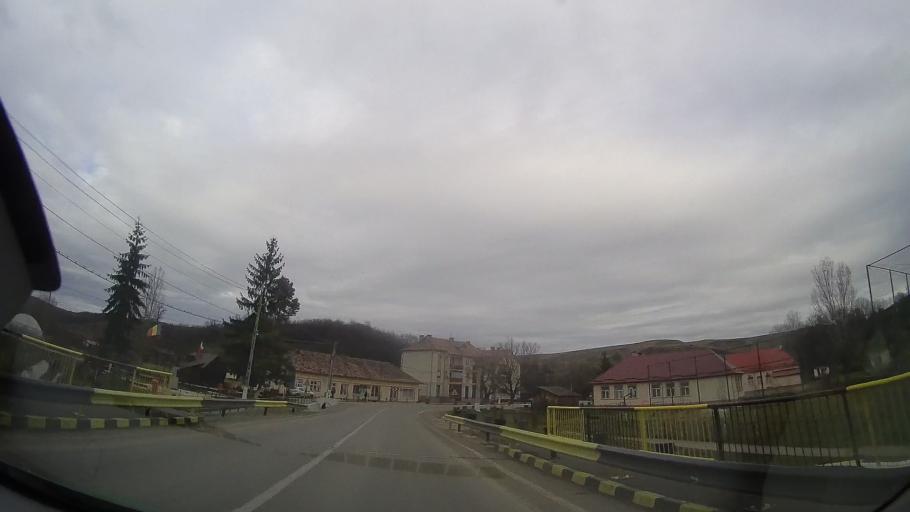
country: RO
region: Mures
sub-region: Comuna Faragau
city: Faragau
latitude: 46.7639
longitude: 24.5162
